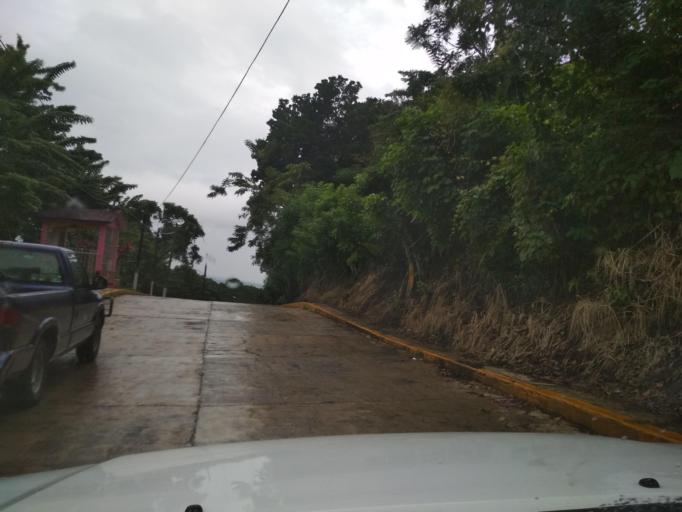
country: MX
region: Veracruz
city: San Andres Tuxtla
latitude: 18.4599
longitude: -95.2100
